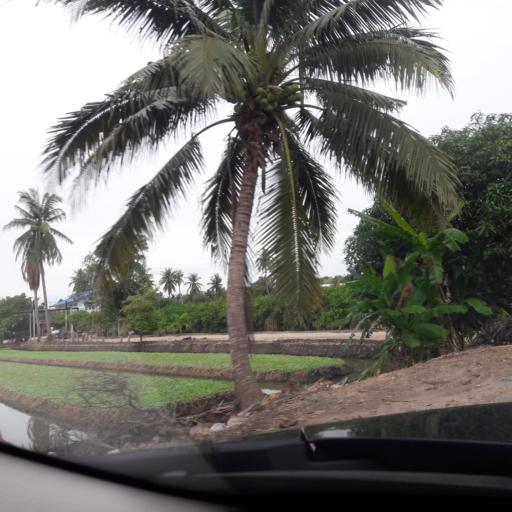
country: TH
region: Ratchaburi
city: Damnoen Saduak
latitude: 13.5604
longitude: 99.9512
